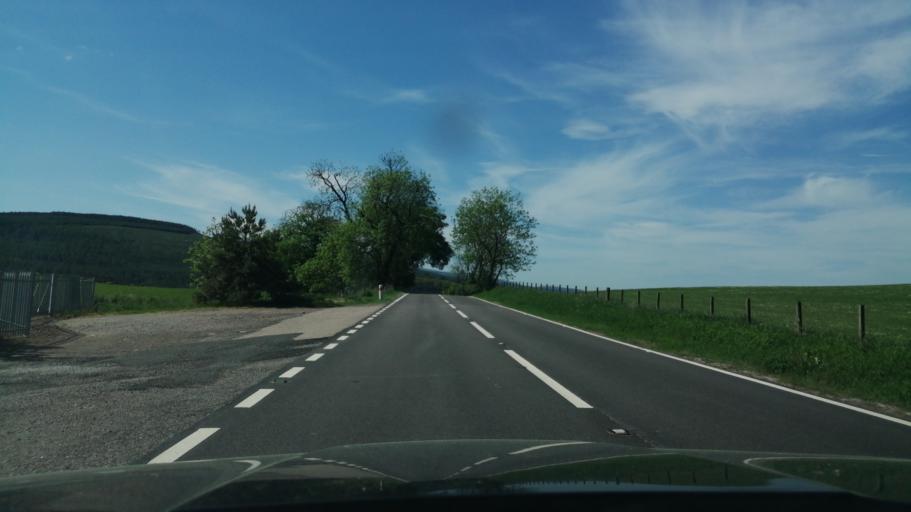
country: GB
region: Scotland
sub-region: Moray
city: Rothes
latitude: 57.4901
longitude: -3.1609
